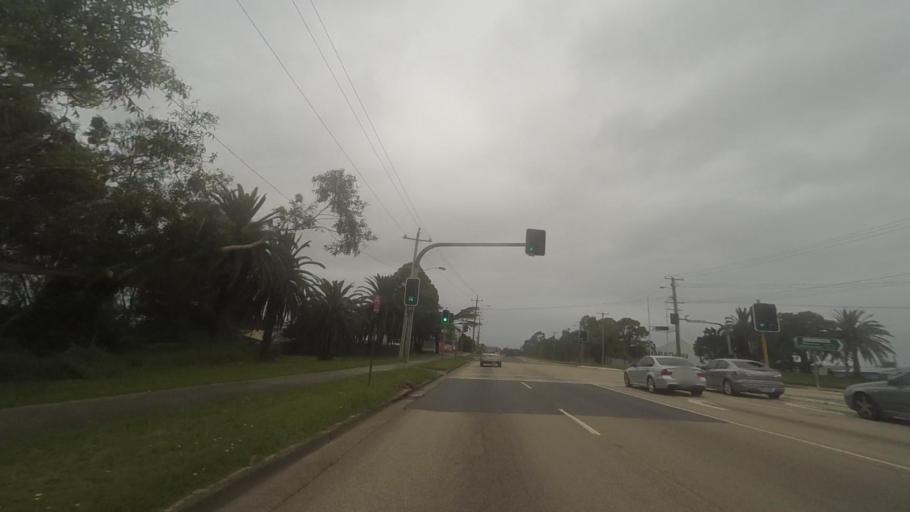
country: AU
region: New South Wales
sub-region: Newcastle
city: Mayfield West
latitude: -32.8705
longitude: 151.7100
